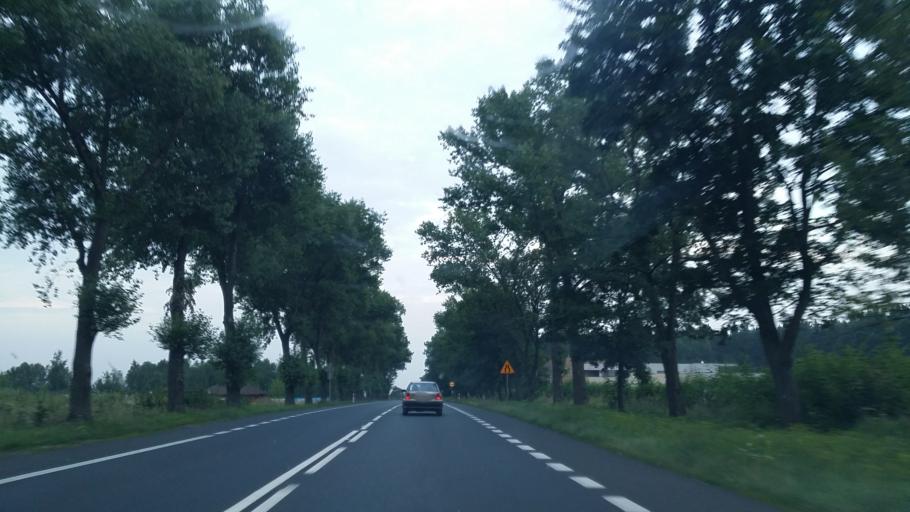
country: PL
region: Lower Silesian Voivodeship
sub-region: Powiat lubinski
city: Osiek
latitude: 51.3832
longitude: 16.2243
